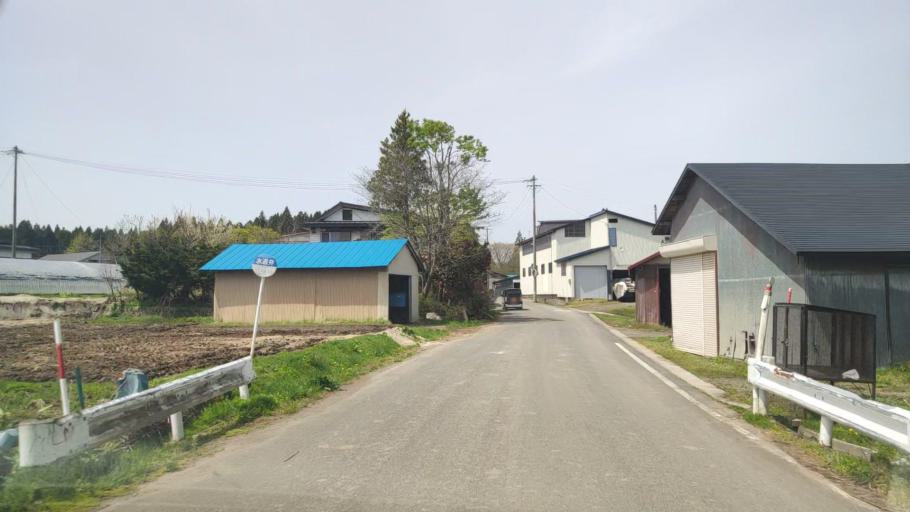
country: JP
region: Aomori
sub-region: Misawa Shi
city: Inuotose
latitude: 40.7791
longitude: 141.1225
